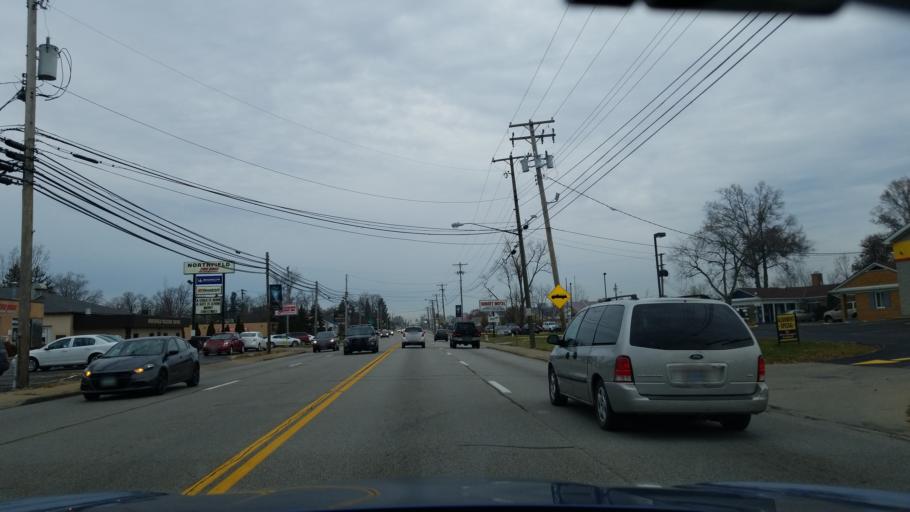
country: US
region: Ohio
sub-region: Summit County
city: Northfield
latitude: 41.3372
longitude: -81.5307
